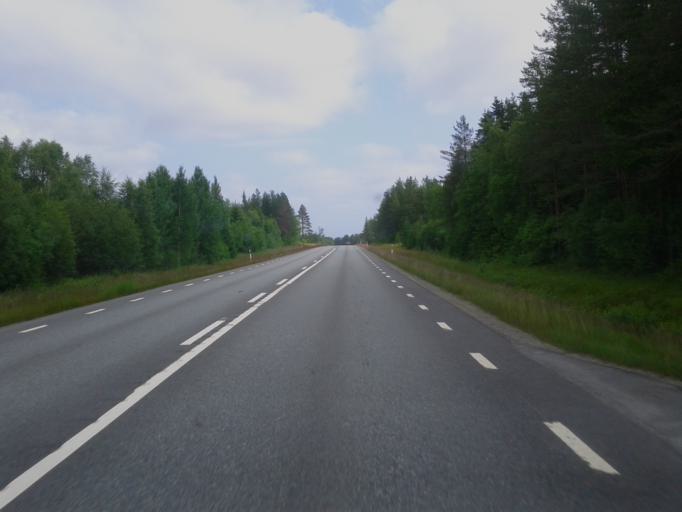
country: SE
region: Vaesterbotten
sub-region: Skelleftea Kommun
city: Burea
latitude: 64.3419
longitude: 21.2805
